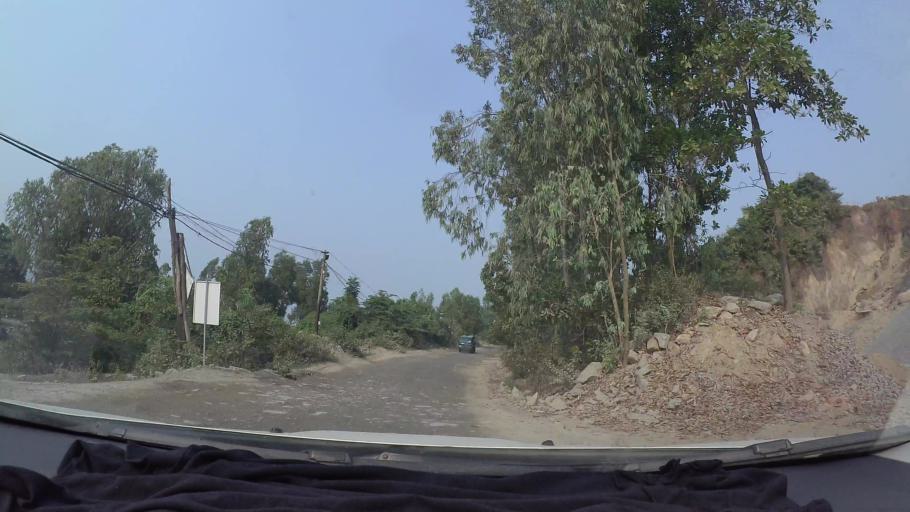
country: VN
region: Da Nang
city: Lien Chieu
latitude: 16.0412
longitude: 108.1601
